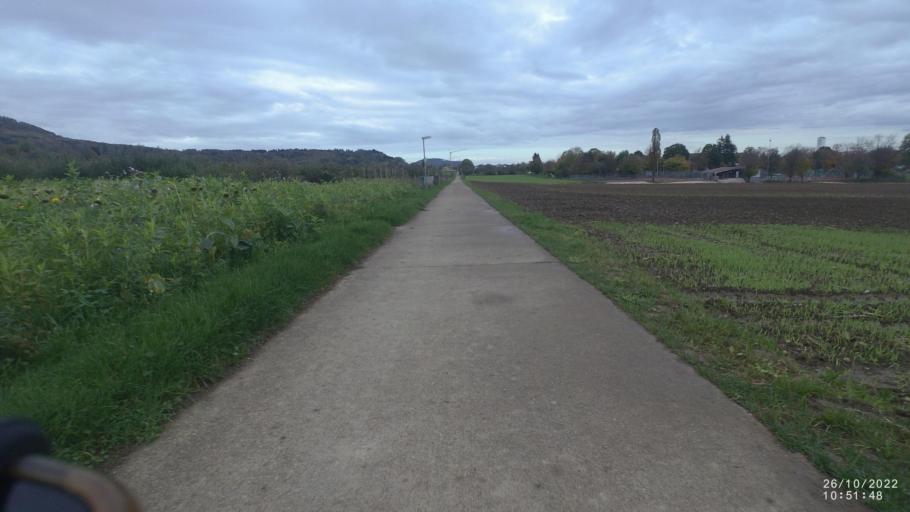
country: DE
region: Baden-Wuerttemberg
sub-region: Regierungsbezirk Stuttgart
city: Gammelshausen
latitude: 48.6406
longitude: 9.6469
